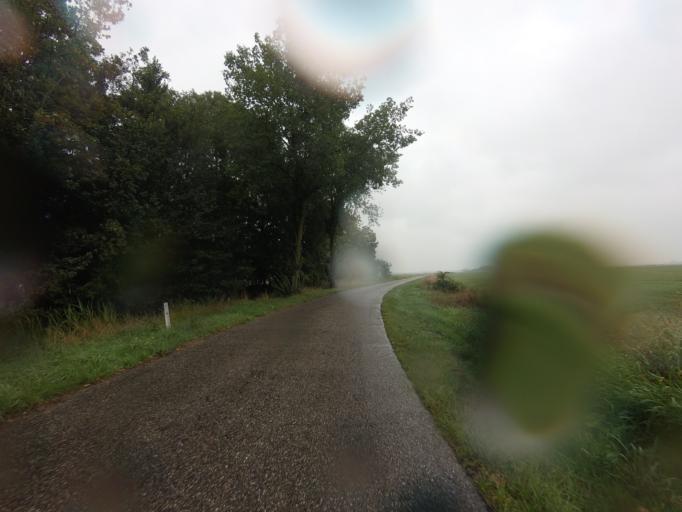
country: NL
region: Friesland
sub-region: Gemeente Boarnsterhim
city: Aldeboarn
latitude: 53.0747
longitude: 5.9285
